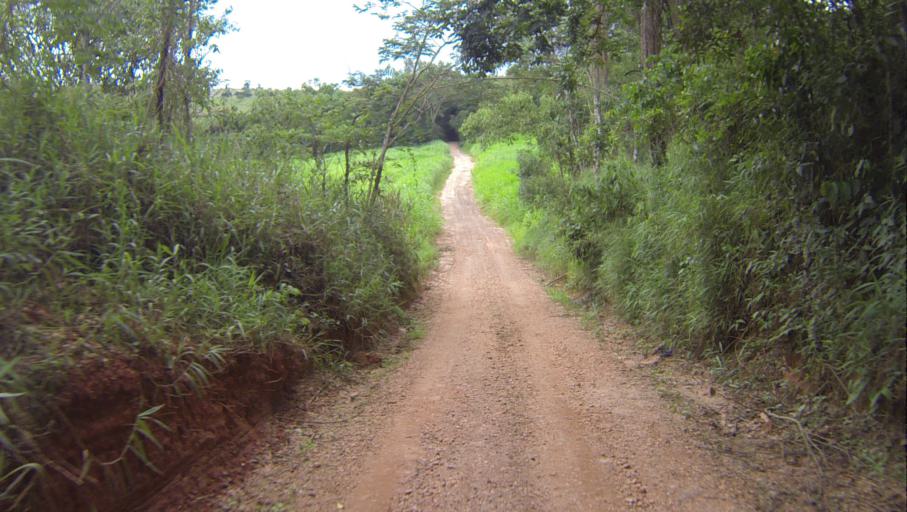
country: BR
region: Minas Gerais
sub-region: Brumadinho
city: Brumadinho
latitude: -20.1579
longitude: -44.1280
